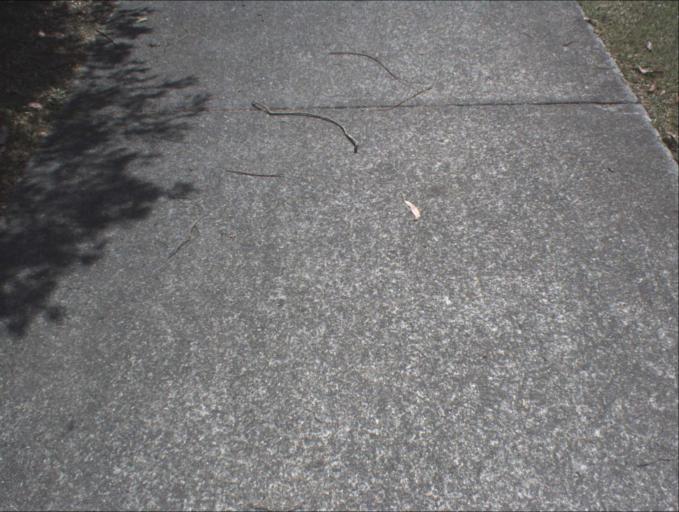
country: AU
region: Queensland
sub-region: Logan
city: Rochedale South
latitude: -27.6051
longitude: 153.1124
